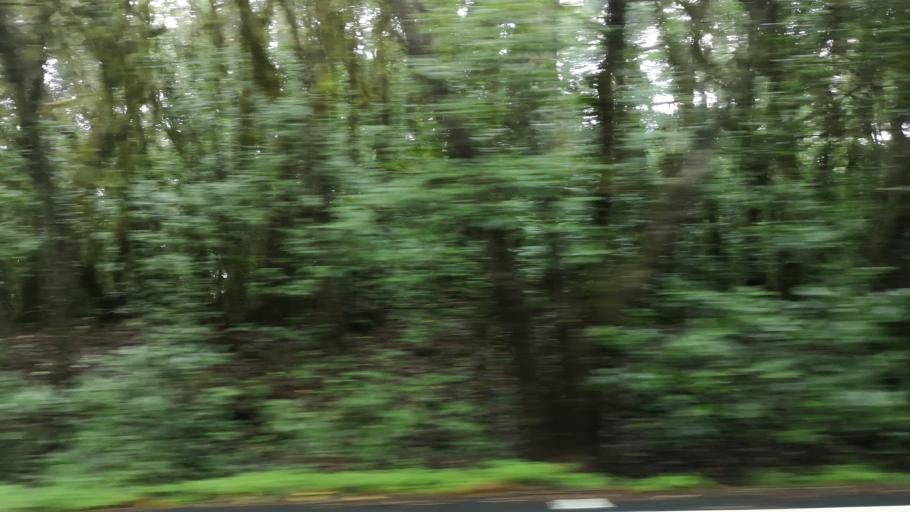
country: ES
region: Canary Islands
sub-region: Provincia de Santa Cruz de Tenerife
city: Vallehermosa
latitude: 28.1517
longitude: -17.2971
